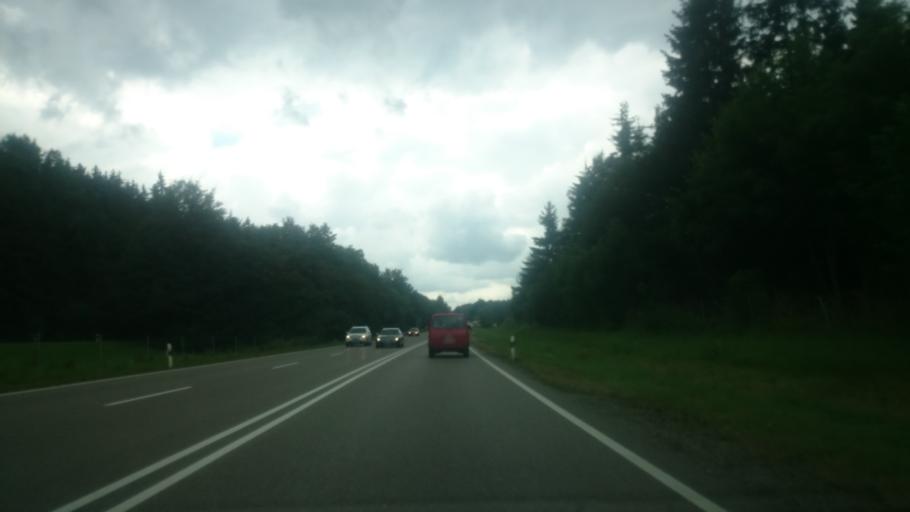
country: DE
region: Bavaria
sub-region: Swabia
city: Mauerstetten
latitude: 47.9078
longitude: 10.6555
